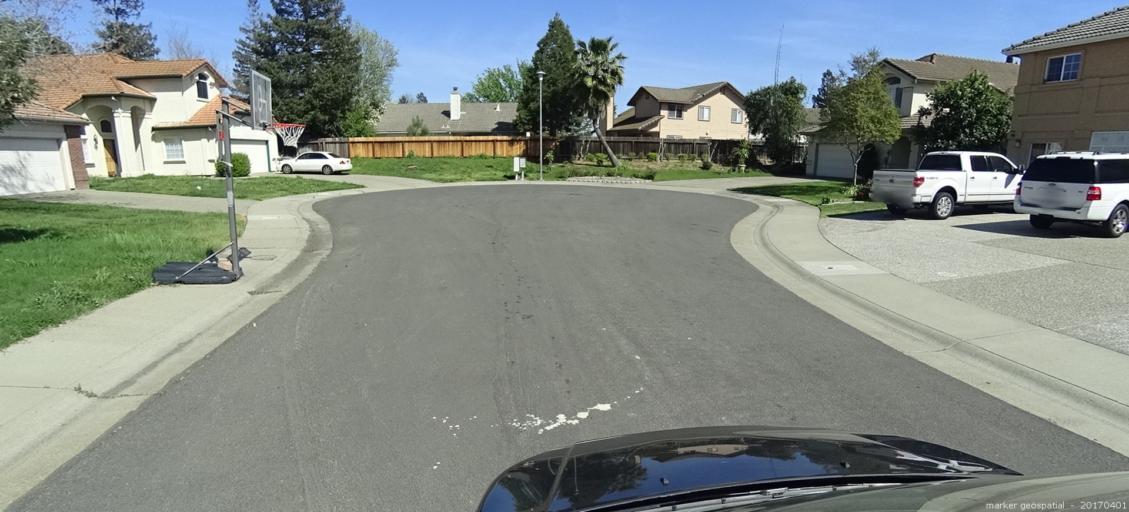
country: US
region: California
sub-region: Sacramento County
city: Laguna
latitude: 38.4456
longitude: -121.4368
